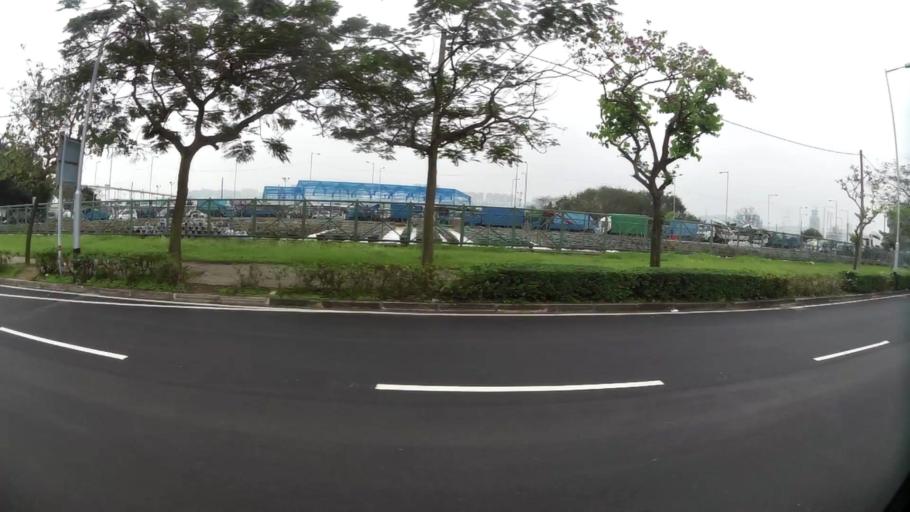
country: MO
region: Macau
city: Macau
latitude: 22.1821
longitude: 113.5406
